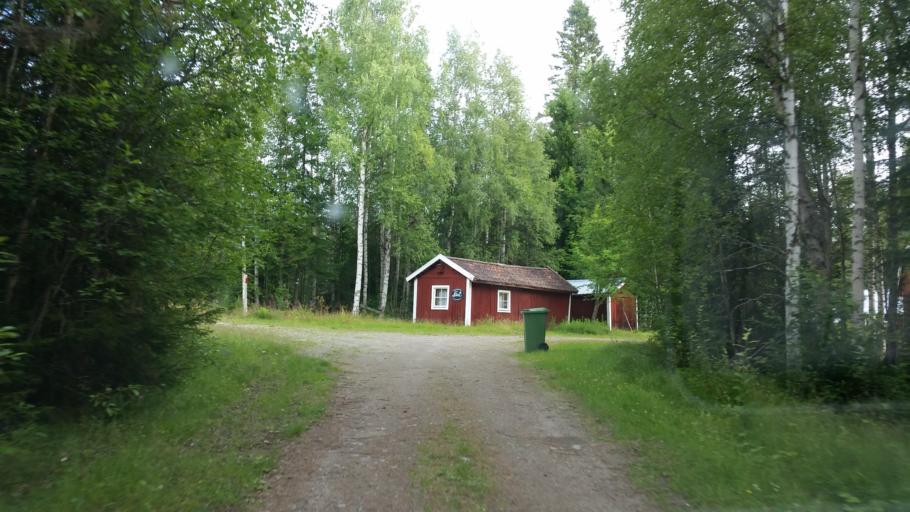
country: SE
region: Vaesternorrland
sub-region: Ange Kommun
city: Ange
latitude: 62.1943
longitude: 15.6474
